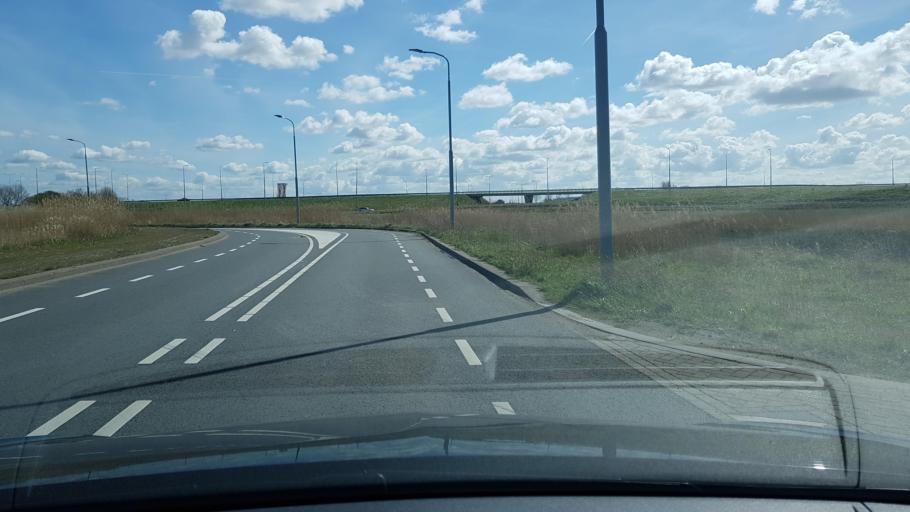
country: NL
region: North Holland
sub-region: Gemeente Haarlem
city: Haarlem
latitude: 52.3721
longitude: 4.6961
